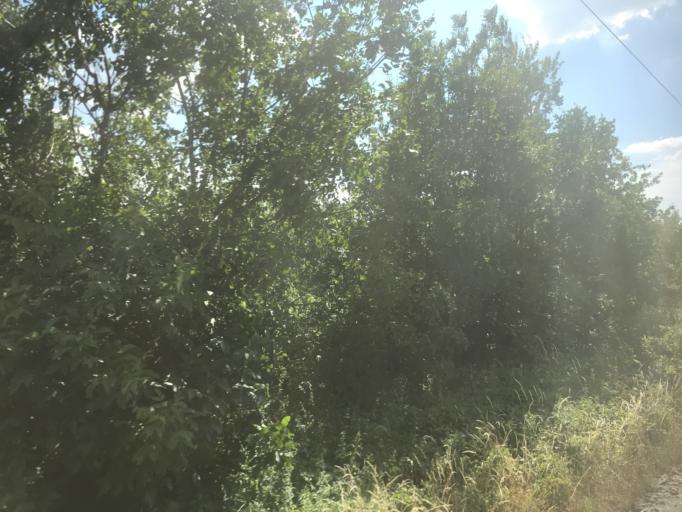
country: AT
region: Upper Austria
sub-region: Politischer Bezirk Urfahr-Umgebung
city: Engerwitzdorf
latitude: 48.3296
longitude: 14.5125
